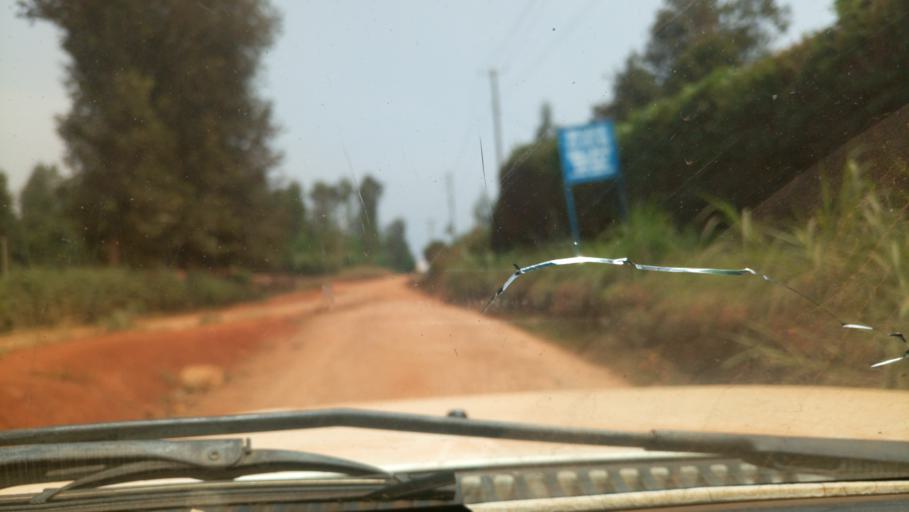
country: KE
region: Murang'a District
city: Kangema
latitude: -0.7393
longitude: 37.0059
